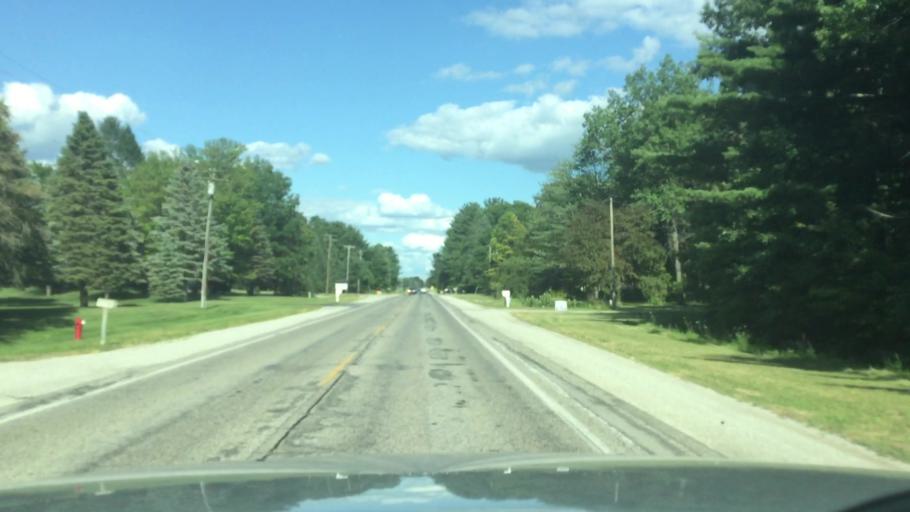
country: US
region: Michigan
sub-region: Saginaw County
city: Shields
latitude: 43.3798
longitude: -84.1264
